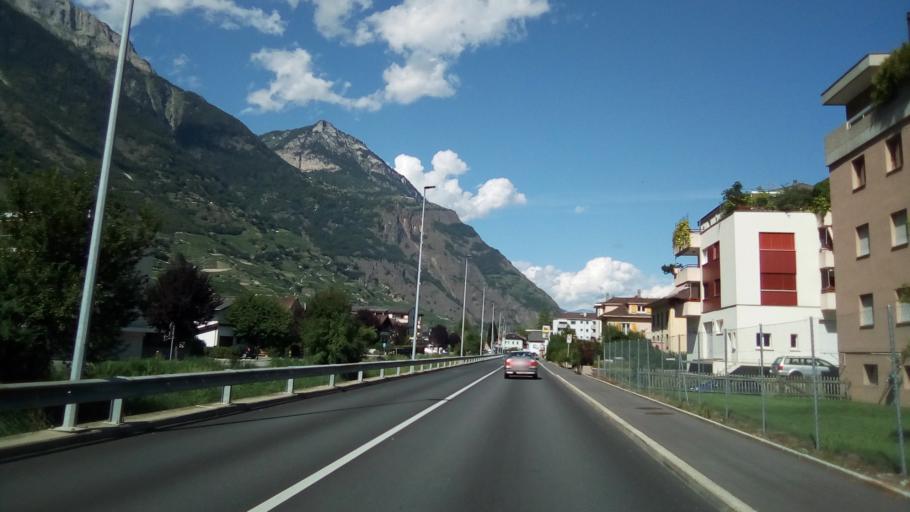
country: CH
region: Valais
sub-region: Martigny District
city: Fully
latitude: 46.1355
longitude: 7.1142
